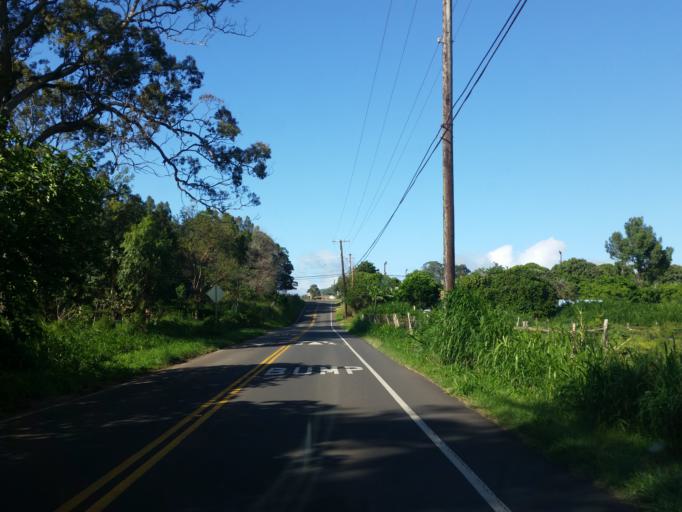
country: US
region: Hawaii
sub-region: Maui County
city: Makawao
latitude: 20.8385
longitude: -156.3089
